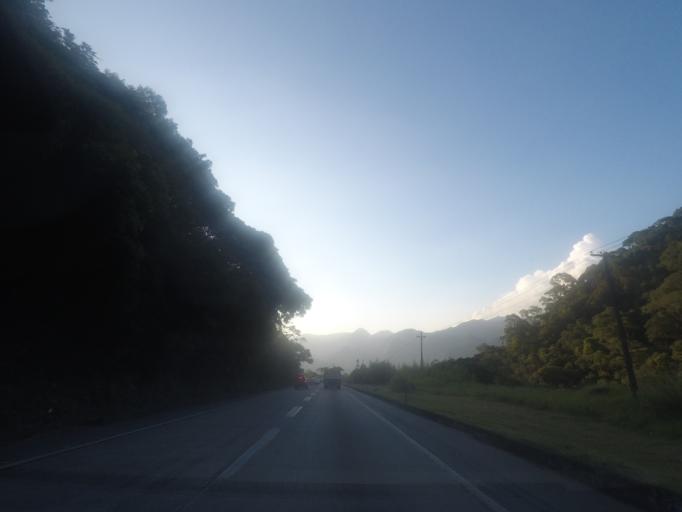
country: BR
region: Rio de Janeiro
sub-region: Petropolis
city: Petropolis
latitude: -22.5218
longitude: -43.2346
